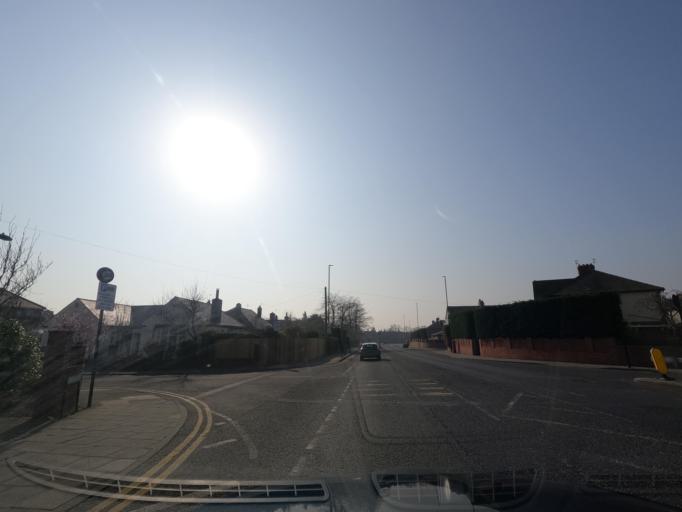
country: GB
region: England
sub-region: Newcastle upon Tyne
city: Gosforth
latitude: 55.0064
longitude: -1.5777
